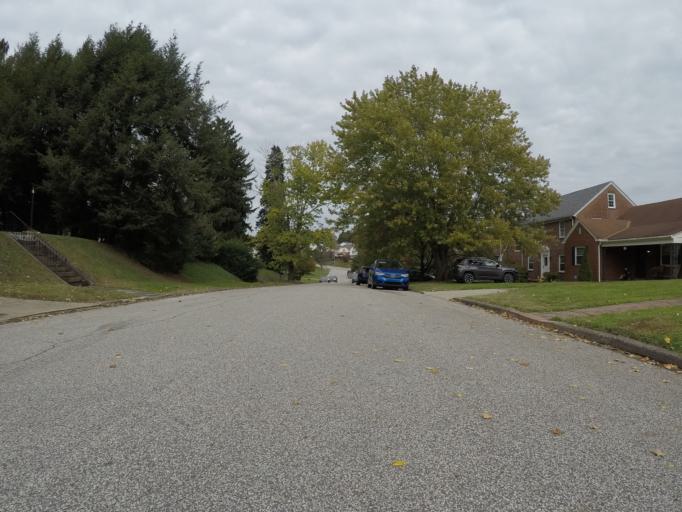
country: US
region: West Virginia
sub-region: Cabell County
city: Huntington
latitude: 38.4065
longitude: -82.4088
